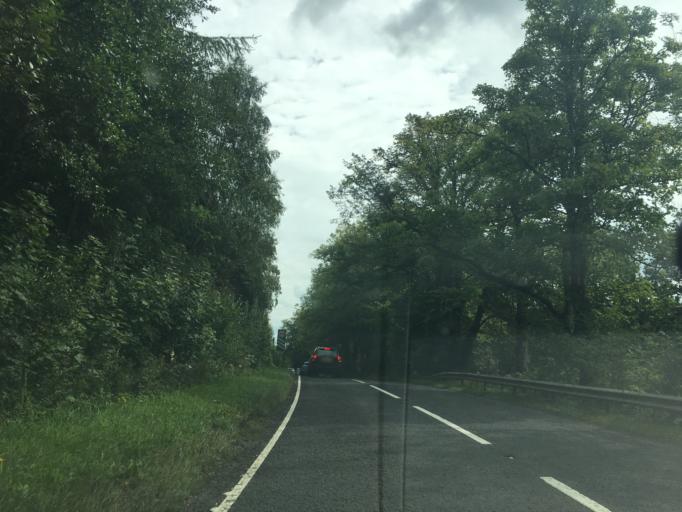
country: GB
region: Scotland
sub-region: Stirling
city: Callander
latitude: 56.2503
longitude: -4.2598
